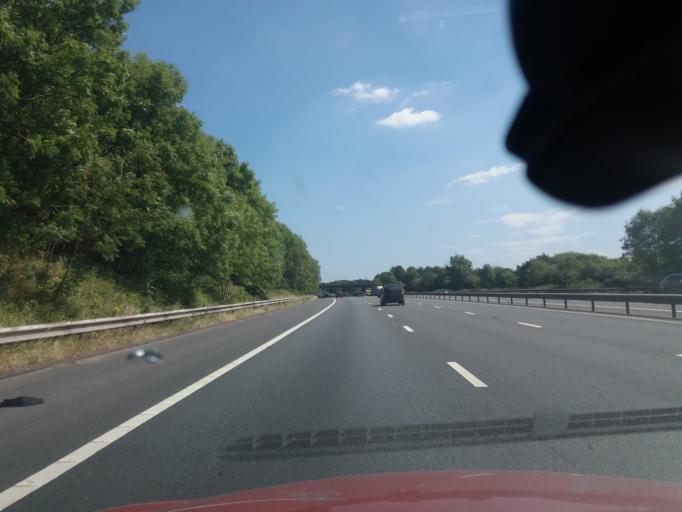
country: GB
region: England
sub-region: Lancashire
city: Chorley
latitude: 53.6366
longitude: -2.5961
